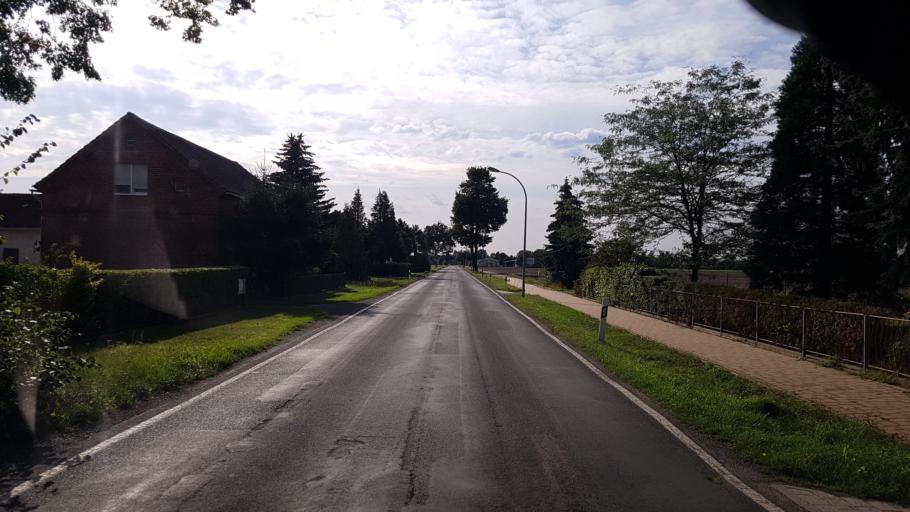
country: DE
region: Brandenburg
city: Welzow
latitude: 51.5510
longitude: 14.2045
